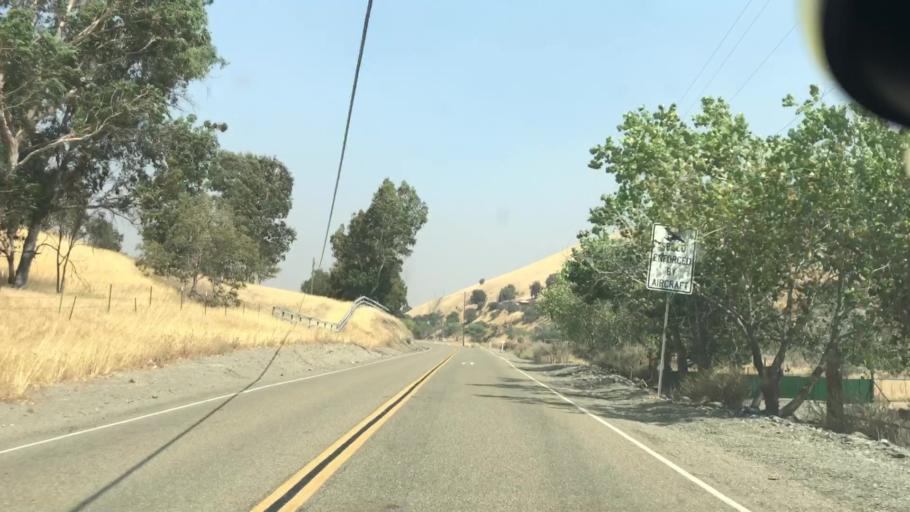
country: US
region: California
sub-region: San Joaquin County
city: Mountain House
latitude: 37.6381
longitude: -121.5785
